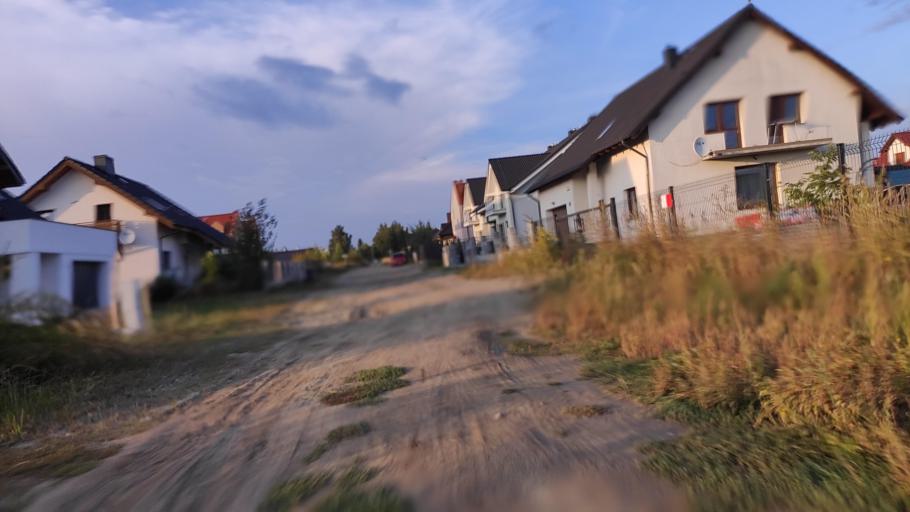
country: PL
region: Greater Poland Voivodeship
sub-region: Powiat poznanski
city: Kleszczewo
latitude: 52.3914
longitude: 17.1630
